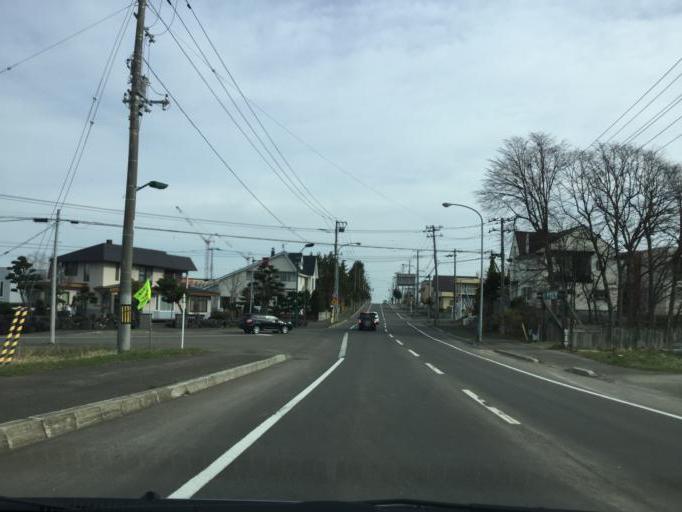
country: JP
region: Hokkaido
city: Iwamizawa
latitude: 43.1789
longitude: 141.7720
